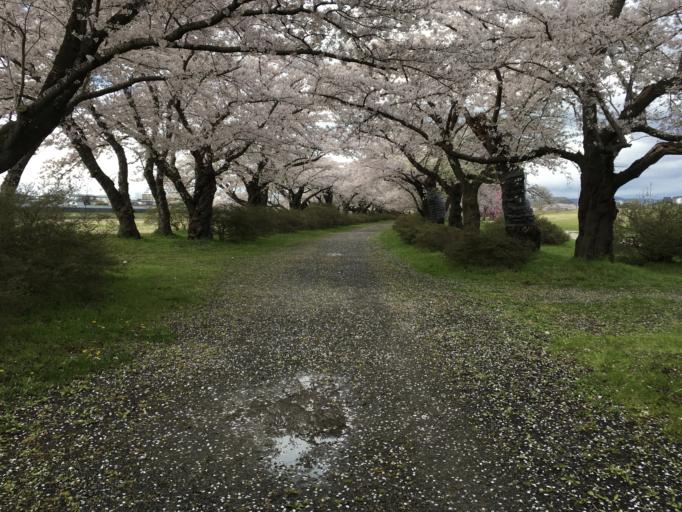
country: JP
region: Iwate
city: Kitakami
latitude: 39.2787
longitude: 141.1276
